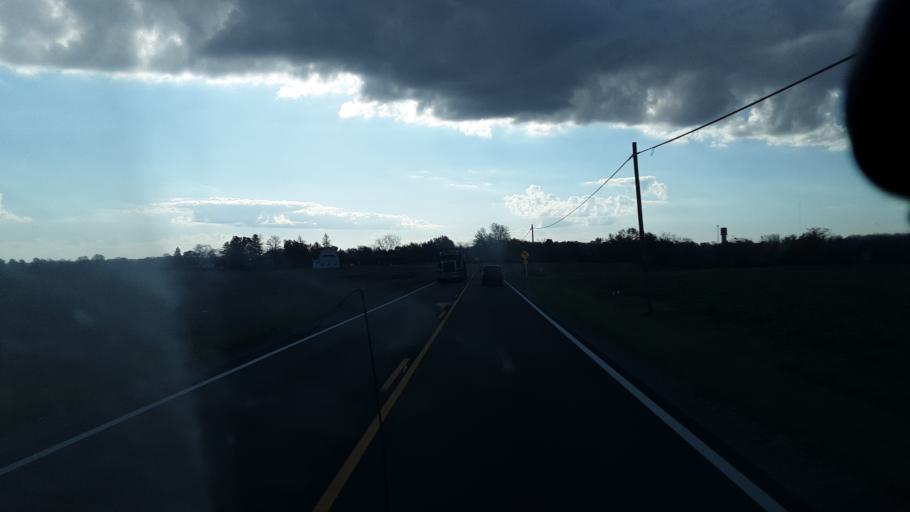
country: US
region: Ohio
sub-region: Fayette County
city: Washington Court House
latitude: 39.5631
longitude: -83.4587
